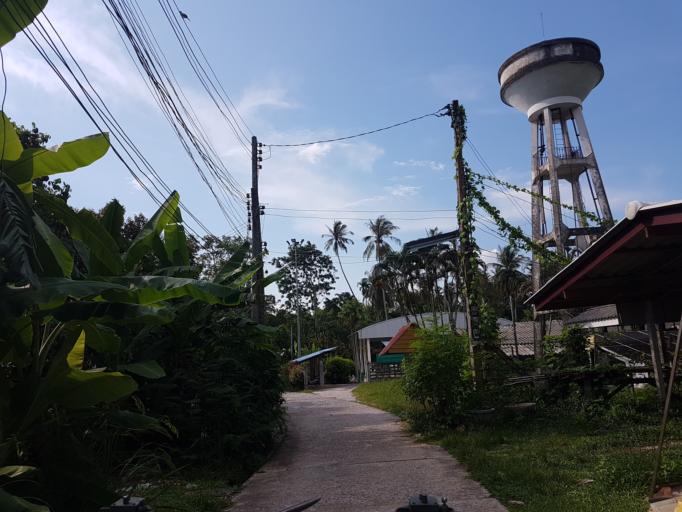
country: TH
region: Pattani
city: Khok Pho
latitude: 6.6718
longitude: 101.1019
